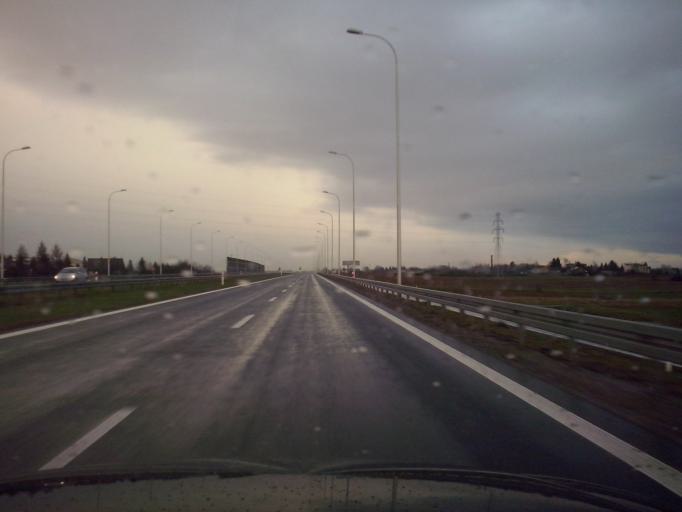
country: PL
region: Lublin Voivodeship
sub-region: Powiat lubelski
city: Jastkow
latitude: 51.2738
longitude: 22.4775
